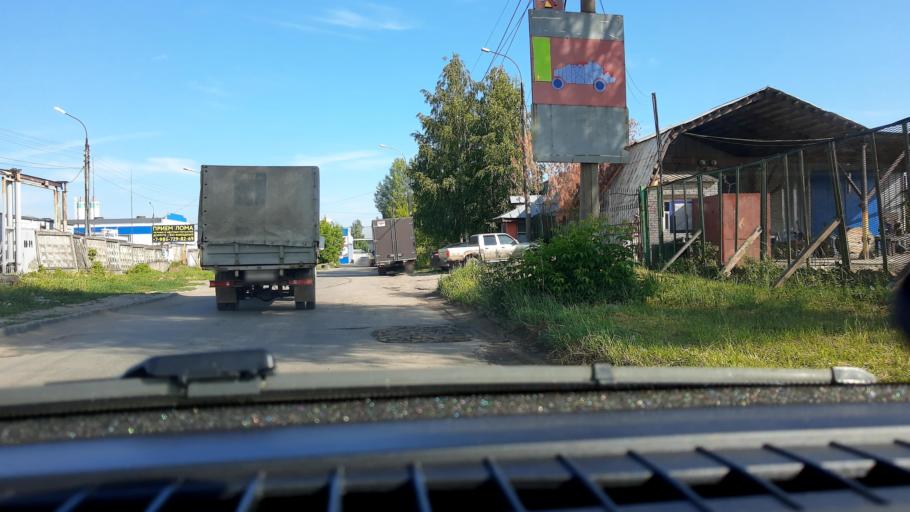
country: RU
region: Nizjnij Novgorod
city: Burevestnik
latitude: 56.2096
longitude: 43.8118
